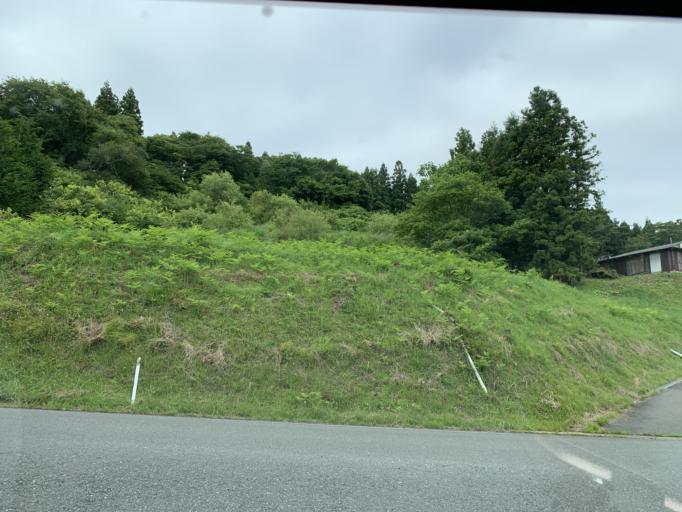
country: JP
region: Iwate
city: Ichinoseki
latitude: 38.8252
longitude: 141.2327
